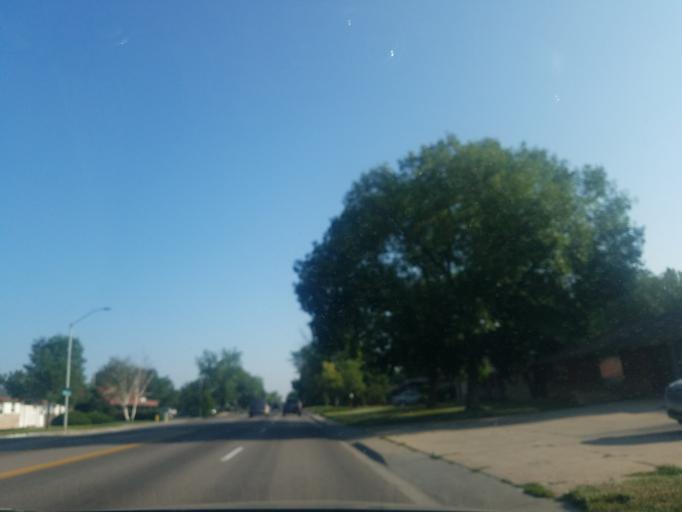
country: US
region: Colorado
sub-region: Larimer County
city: Fort Collins
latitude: 40.5720
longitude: -105.1150
